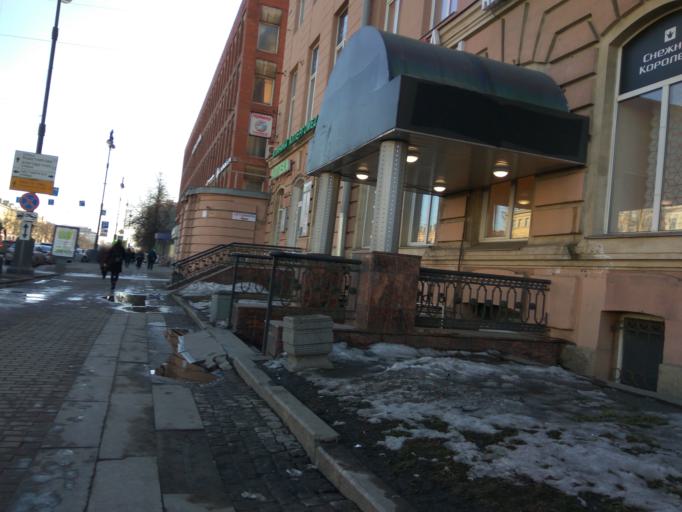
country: RU
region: St.-Petersburg
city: Admiralteisky
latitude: 59.8896
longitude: 30.3190
